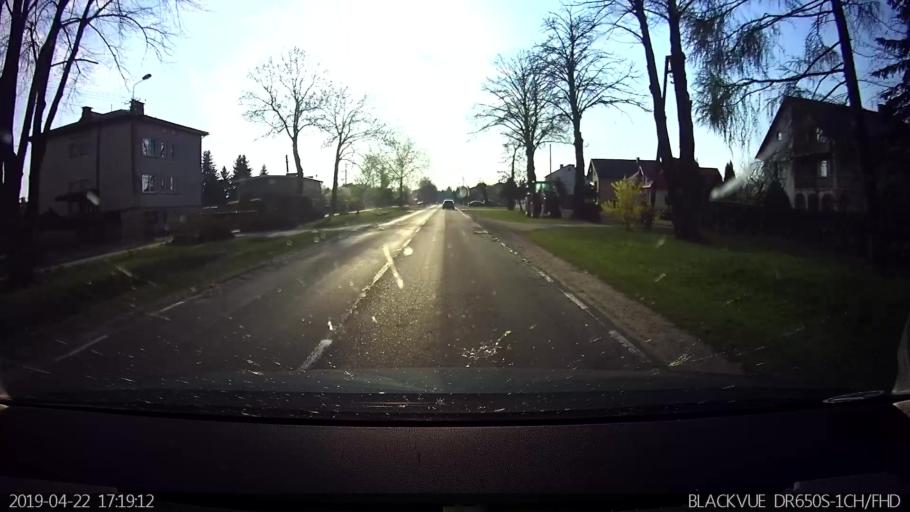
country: PL
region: Masovian Voivodeship
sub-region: Powiat sokolowski
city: Repki
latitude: 52.3850
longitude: 22.3977
